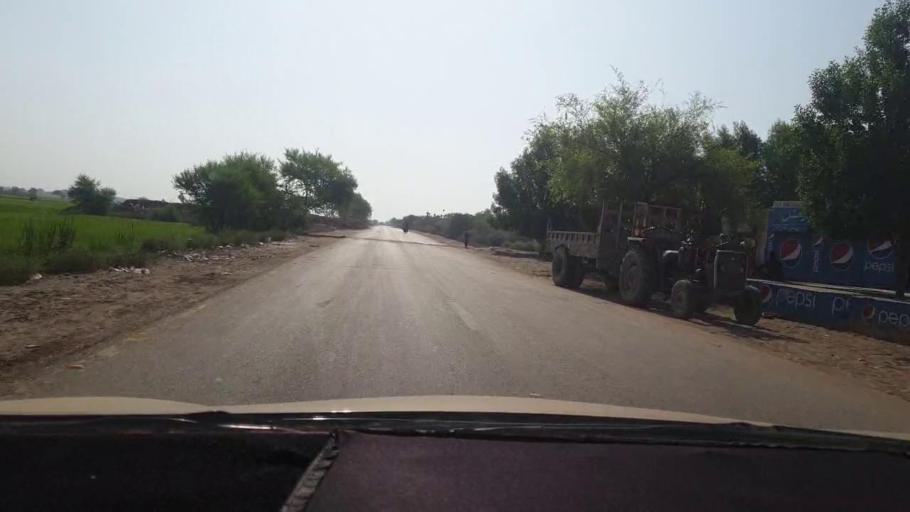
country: PK
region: Sindh
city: Miro Khan
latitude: 27.7333
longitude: 68.1186
